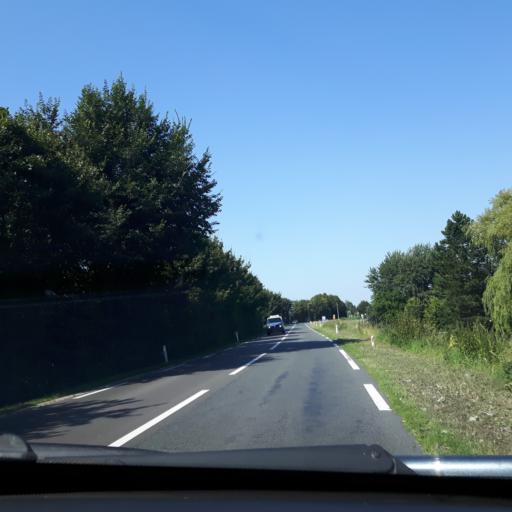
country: NL
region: Zeeland
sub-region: Gemeente Reimerswaal
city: Yerseke
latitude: 51.4790
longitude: 4.0475
